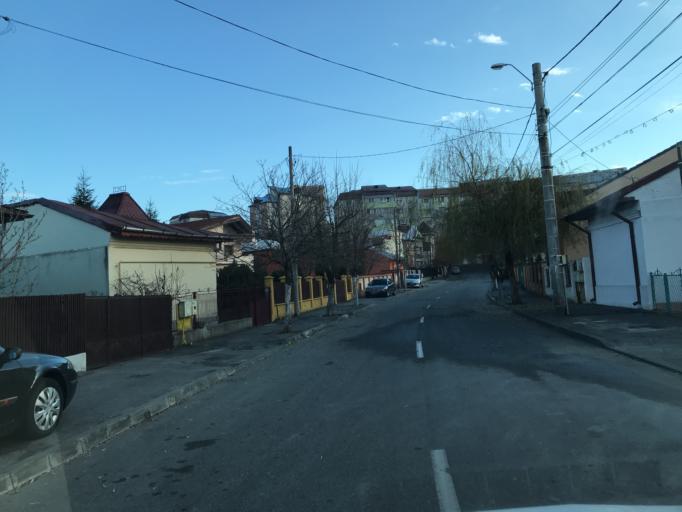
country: RO
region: Olt
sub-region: Municipiul Slatina
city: Slatina
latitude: 44.4332
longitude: 24.3546
